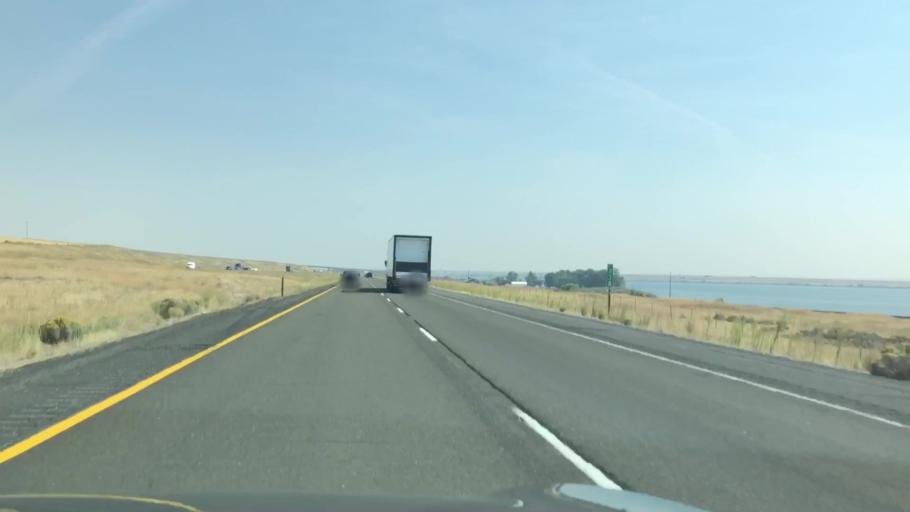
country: US
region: Washington
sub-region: Adams County
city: Ritzville
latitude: 47.2526
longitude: -118.0974
